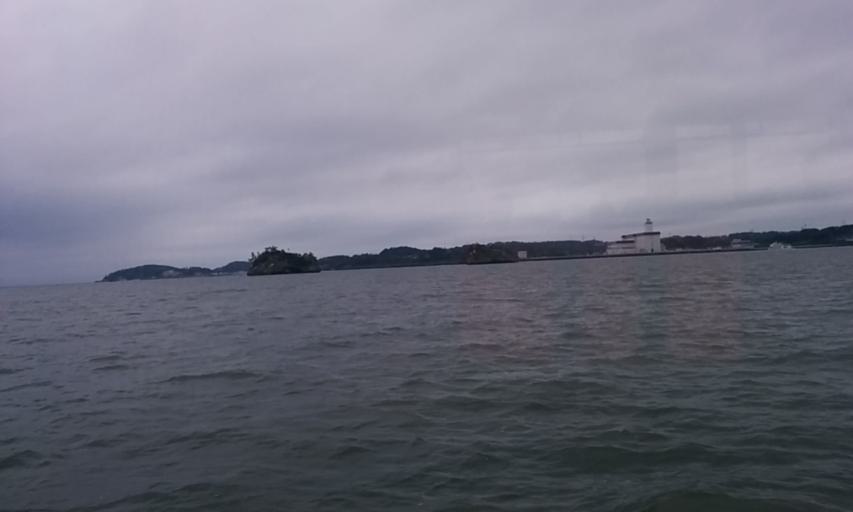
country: JP
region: Miyagi
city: Shiogama
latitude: 38.3287
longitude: 141.0796
